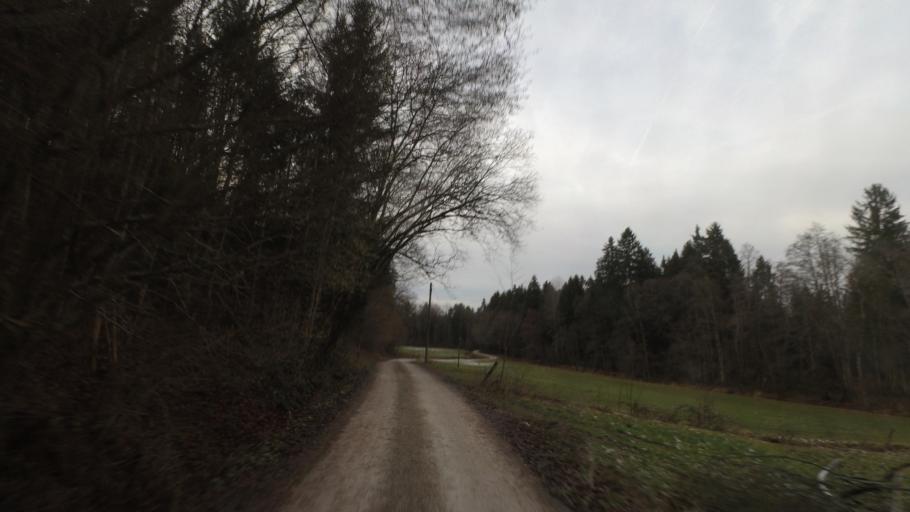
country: DE
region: Bavaria
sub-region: Upper Bavaria
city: Ubersee
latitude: 47.8096
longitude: 12.5167
